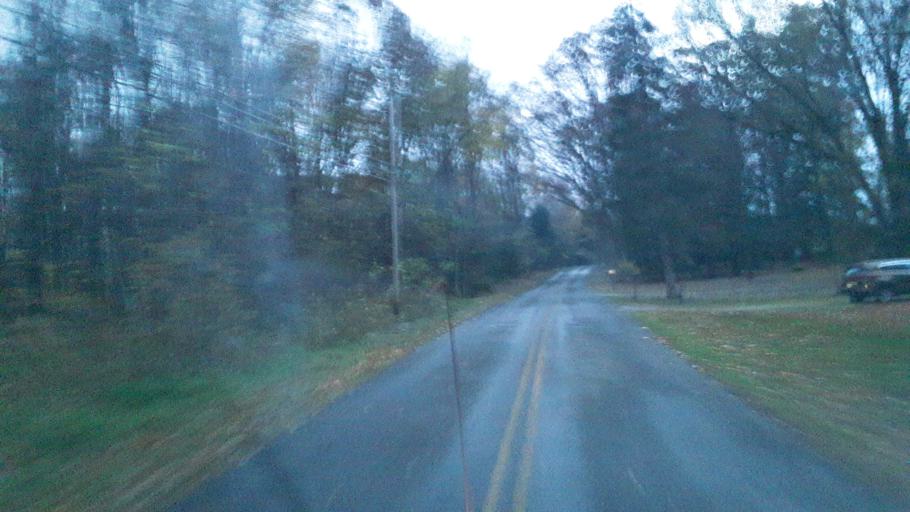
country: US
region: Ohio
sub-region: Portage County
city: Mantua
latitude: 41.3162
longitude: -81.2408
